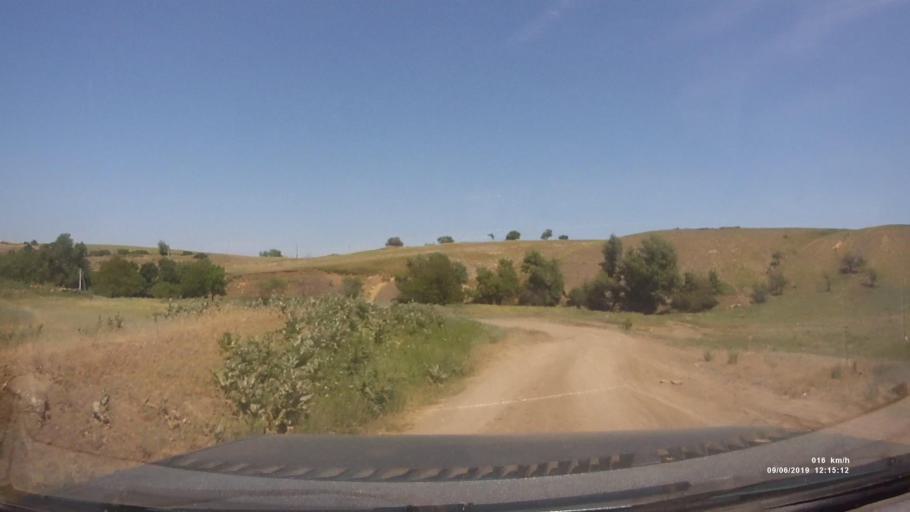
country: RU
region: Rostov
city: Staraya Stanitsa
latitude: 48.2539
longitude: 40.3228
